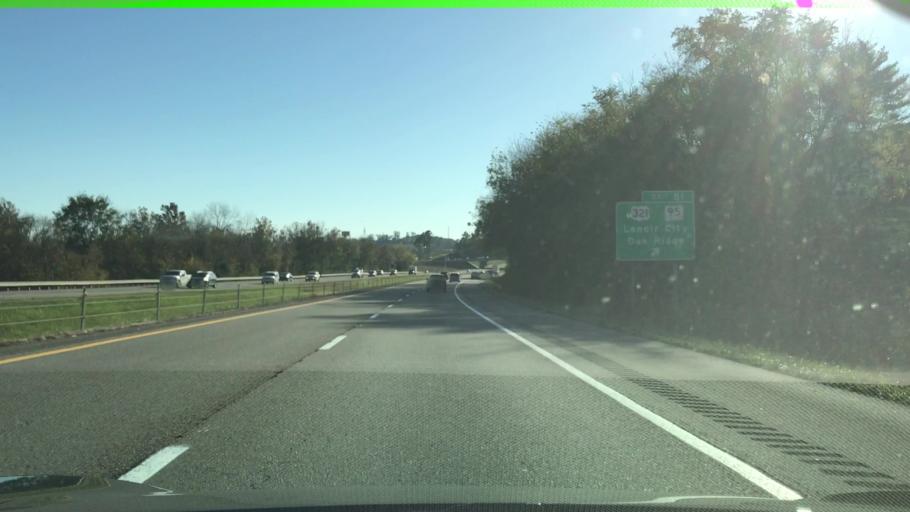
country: US
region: Tennessee
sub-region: Loudon County
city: Lenoir City
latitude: 35.8334
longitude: -84.2755
